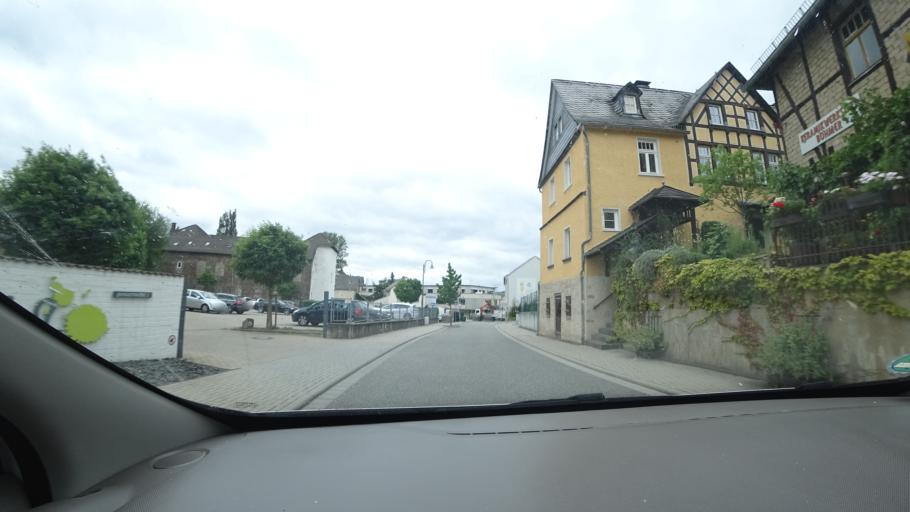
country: DE
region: Rheinland-Pfalz
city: Hohr-Grenzhausen
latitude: 50.4324
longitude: 7.6752
